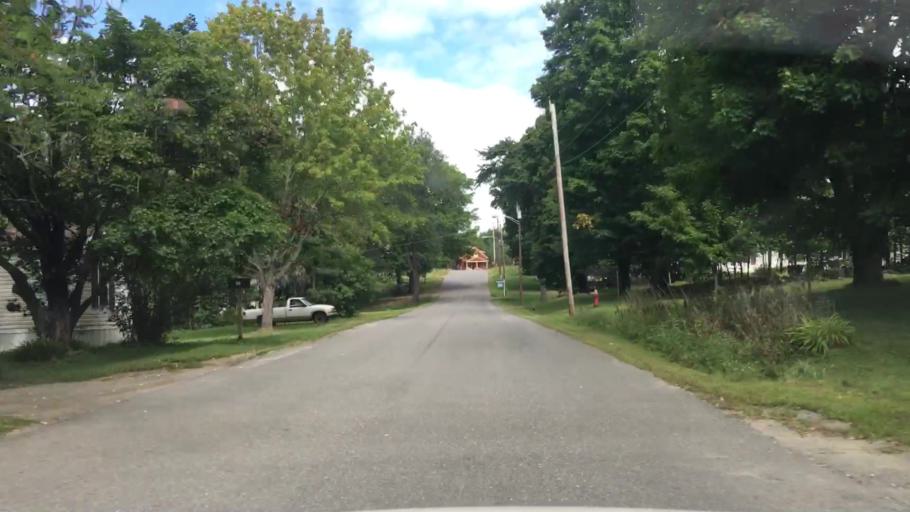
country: US
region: Maine
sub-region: Piscataquis County
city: Dover-Foxcroft
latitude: 45.1891
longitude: -69.2227
